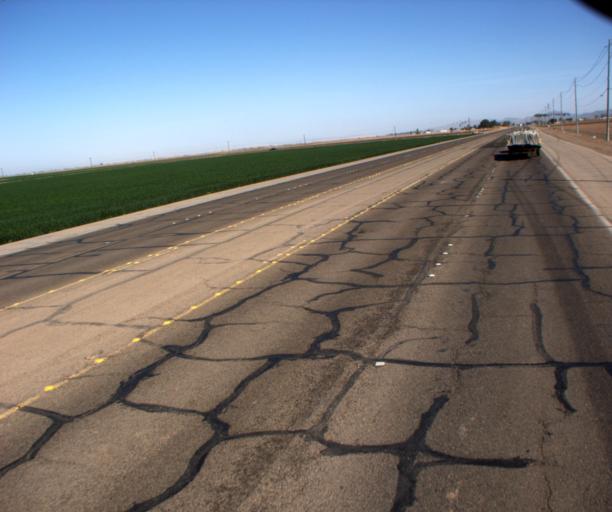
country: US
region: Arizona
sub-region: Yuma County
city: Somerton
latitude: 32.5783
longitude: -114.7698
